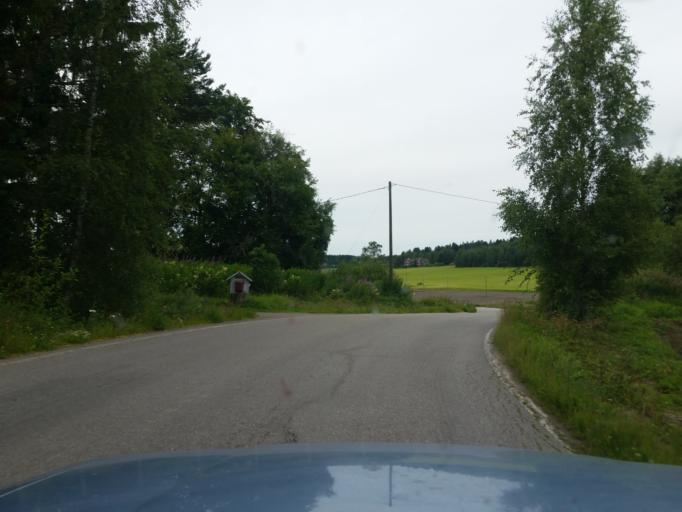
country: FI
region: Uusimaa
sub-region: Helsinki
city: Sammatti
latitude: 60.4732
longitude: 23.8239
